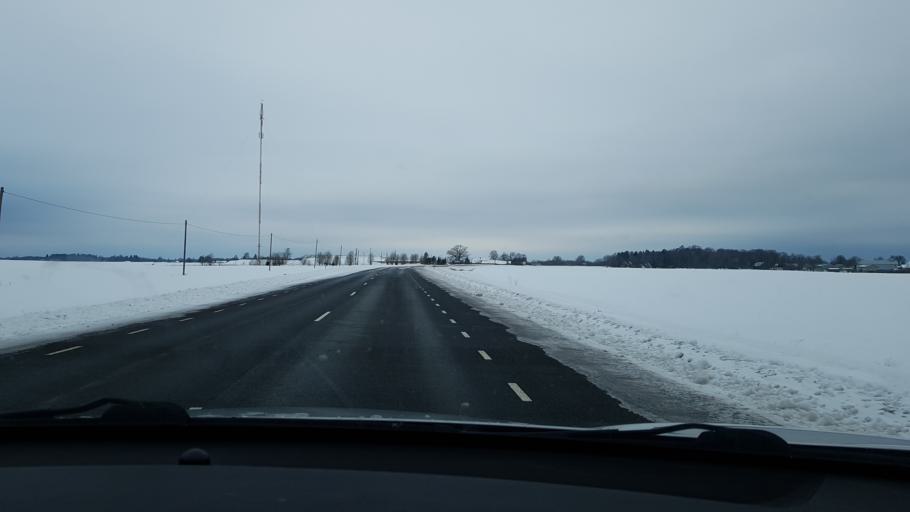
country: EE
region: Jaervamaa
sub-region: Jaerva-Jaani vald
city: Jarva-Jaani
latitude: 58.8962
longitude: 25.7635
